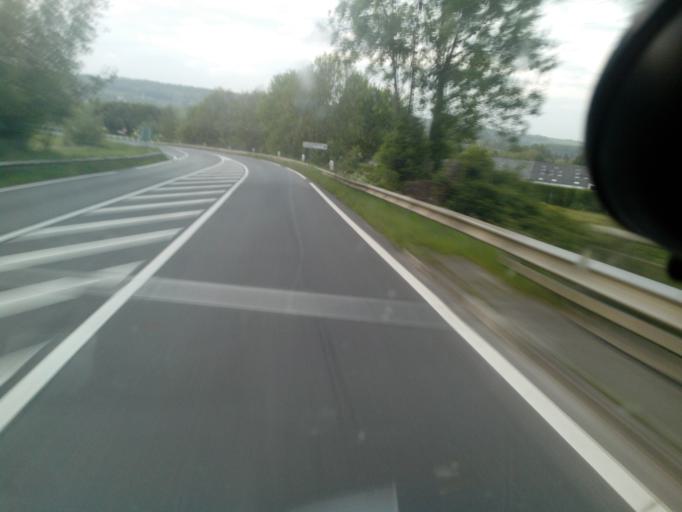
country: FR
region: Nord-Pas-de-Calais
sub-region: Departement du Pas-de-Calais
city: Hesdin
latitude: 50.3617
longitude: 2.0390
